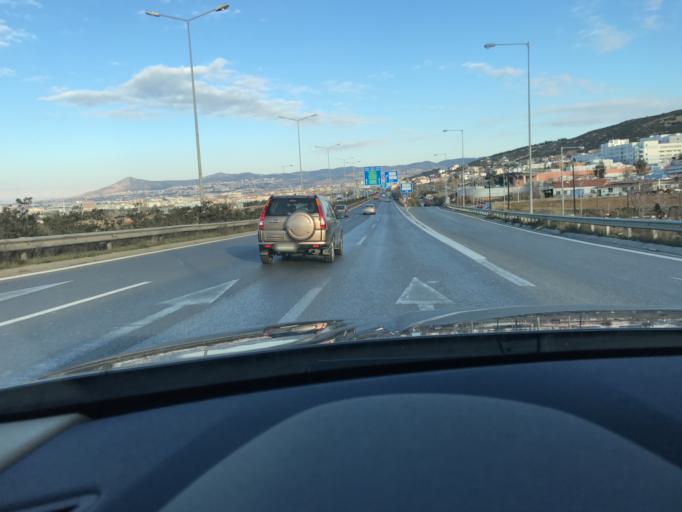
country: GR
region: Central Macedonia
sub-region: Nomos Thessalonikis
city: Polichni
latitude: 40.6701
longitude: 22.9619
